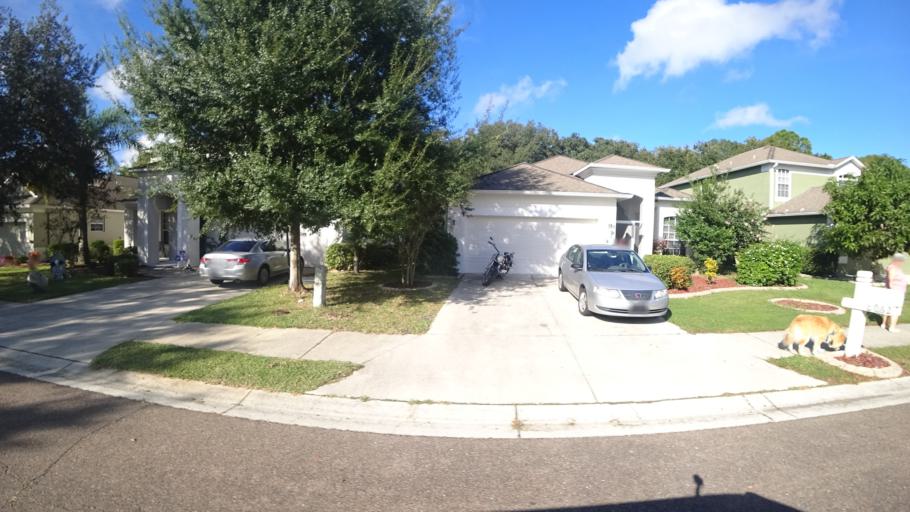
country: US
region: Florida
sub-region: Manatee County
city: Ellenton
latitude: 27.5896
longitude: -82.5018
